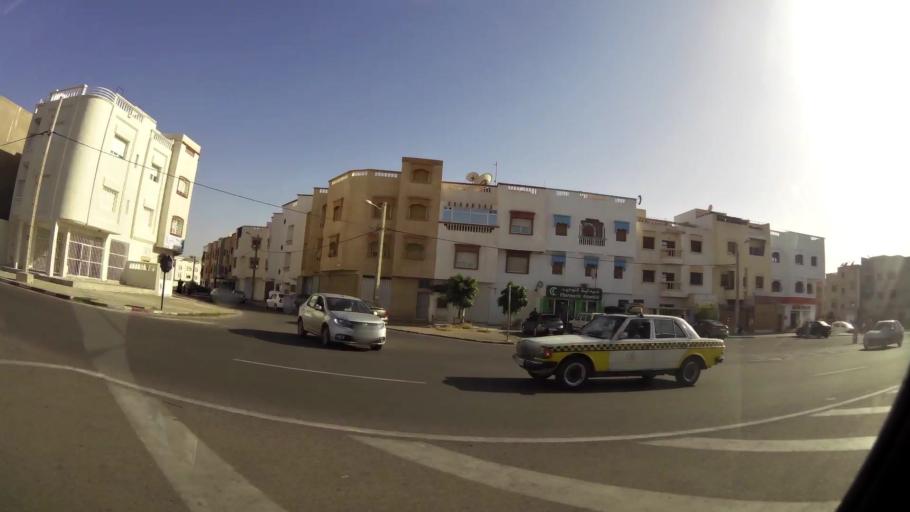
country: MA
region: Oued ed Dahab-Lagouira
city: Dakhla
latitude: 30.3952
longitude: -9.5376
